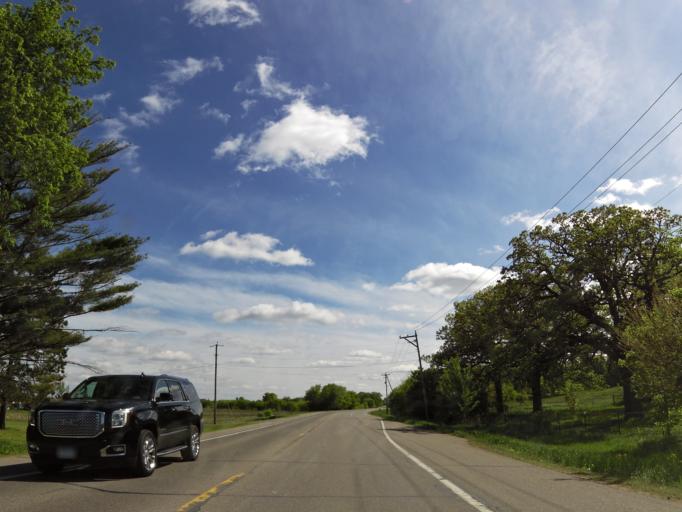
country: US
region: Minnesota
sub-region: Washington County
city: Lakeland
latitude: 44.9775
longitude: -92.7918
